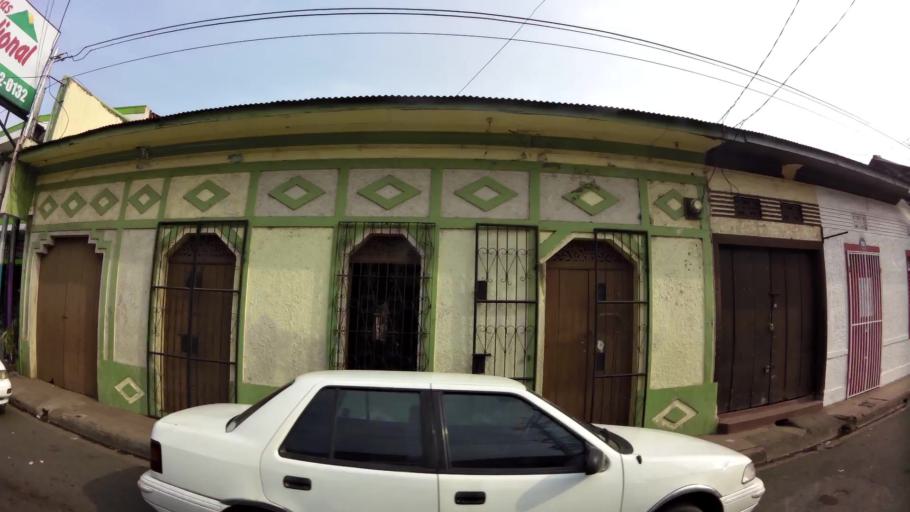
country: NI
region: Masaya
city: Masaya
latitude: 11.9752
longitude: -86.0928
